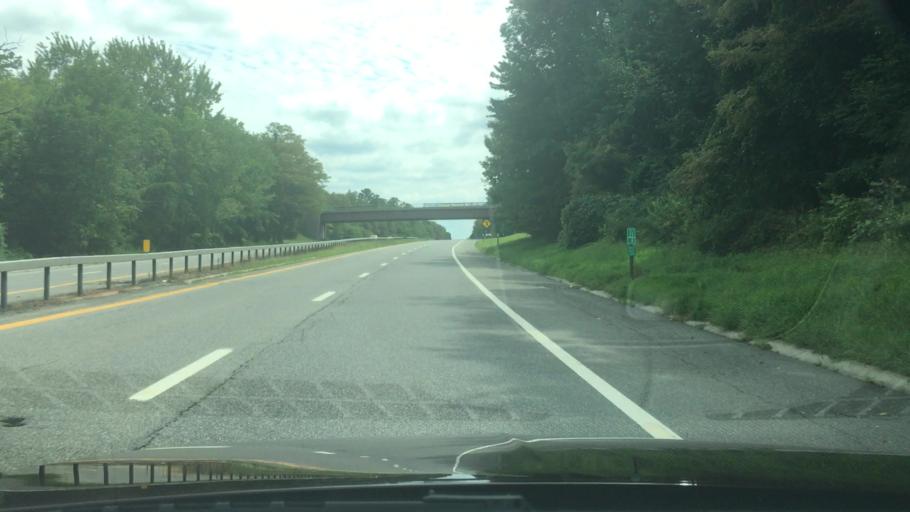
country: US
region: New York
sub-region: Westchester County
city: Shrub Oak
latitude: 41.3765
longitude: -73.7999
